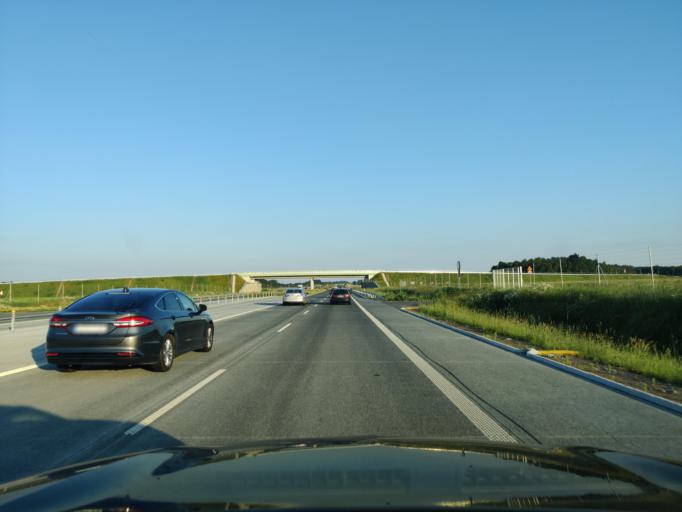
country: PL
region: Masovian Voivodeship
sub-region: Powiat mlawski
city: Strzegowo
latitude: 52.8795
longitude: 20.2713
